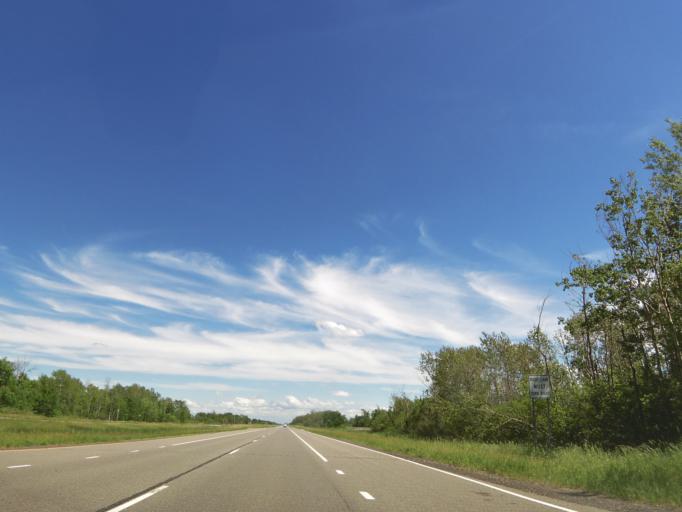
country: US
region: Minnesota
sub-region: Todd County
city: Staples
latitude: 46.3667
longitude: -94.8860
